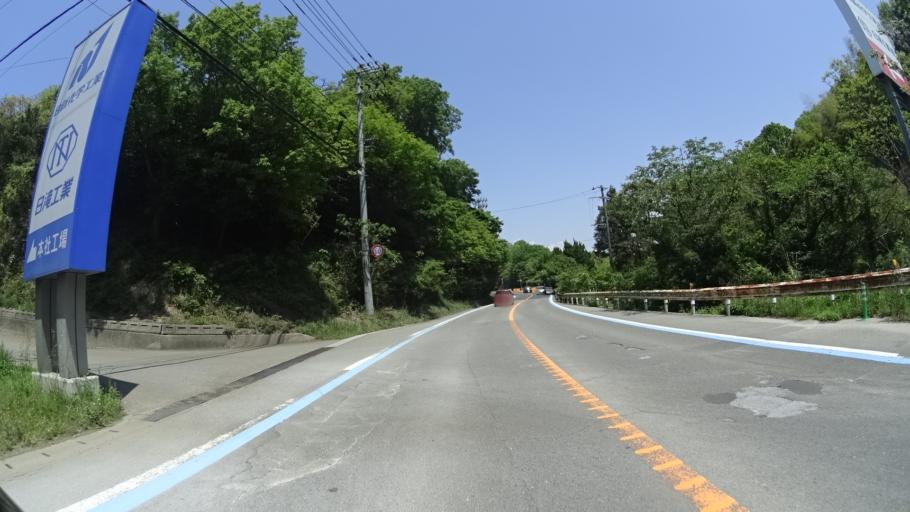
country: JP
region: Ehime
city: Iyo
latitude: 33.7150
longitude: 132.6742
